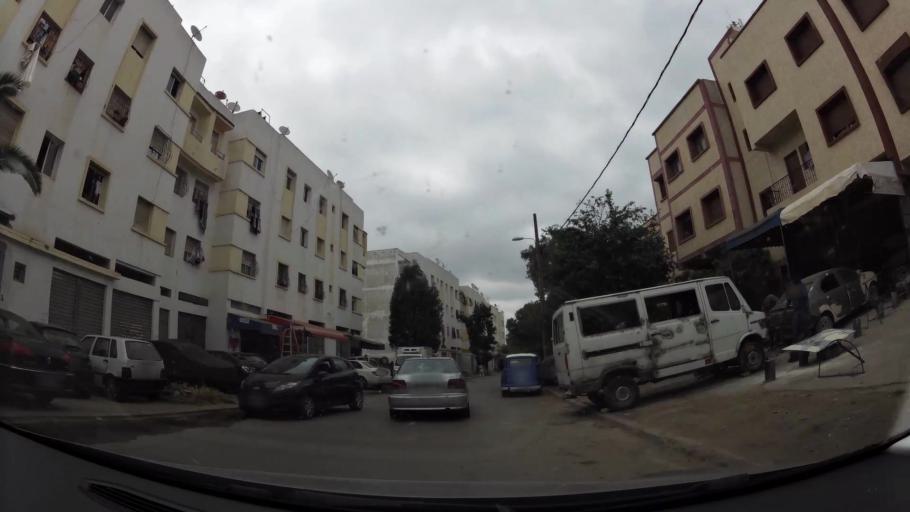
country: MA
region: Rabat-Sale-Zemmour-Zaer
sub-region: Rabat
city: Rabat
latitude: 33.9830
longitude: -6.8139
